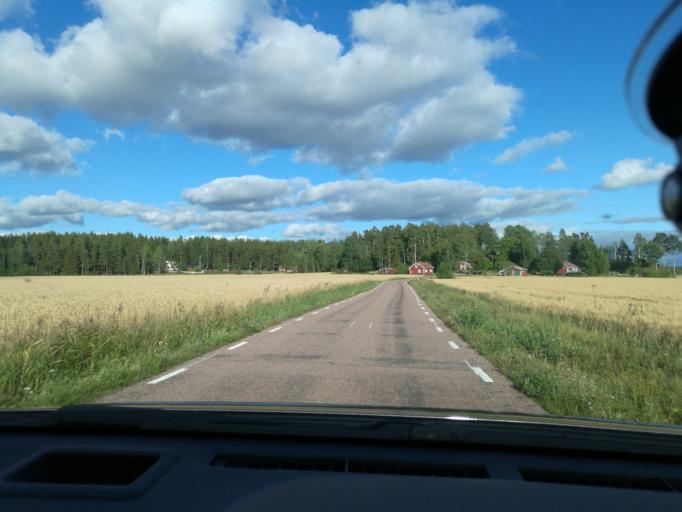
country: SE
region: Vaestmanland
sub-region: Kopings Kommun
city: Koping
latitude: 59.5474
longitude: 16.1134
